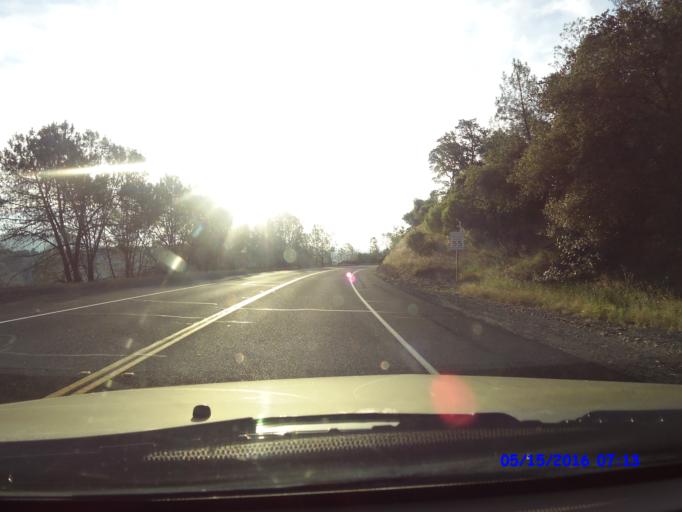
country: US
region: California
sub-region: Tuolumne County
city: Jamestown
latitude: 37.8400
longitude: -120.3717
